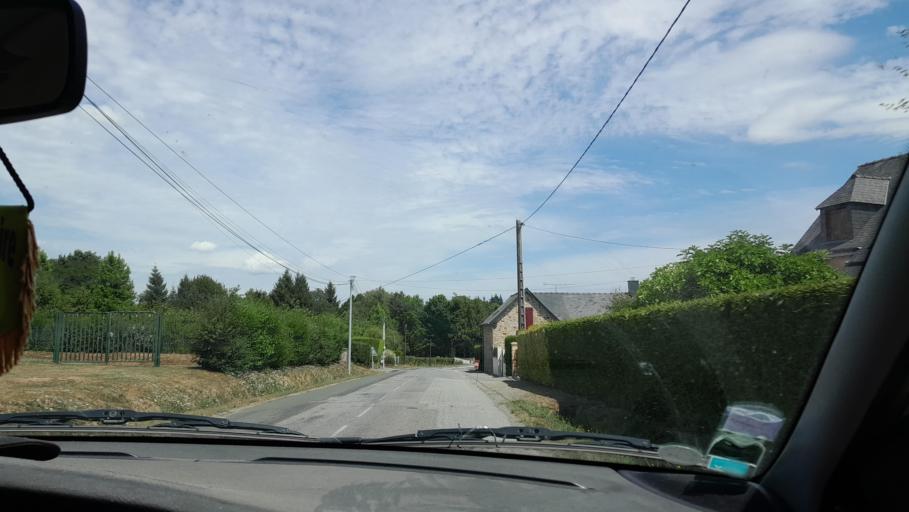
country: FR
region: Brittany
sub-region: Departement d'Ille-et-Vilaine
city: Le Pertre
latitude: 48.0689
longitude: -1.0211
